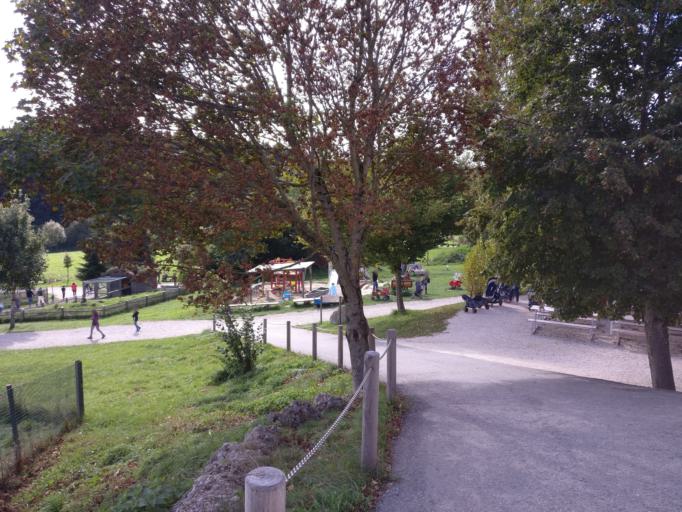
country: DE
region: Bavaria
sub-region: Upper Bavaria
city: Feldkirchen-Westerham
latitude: 47.9299
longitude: 11.8134
